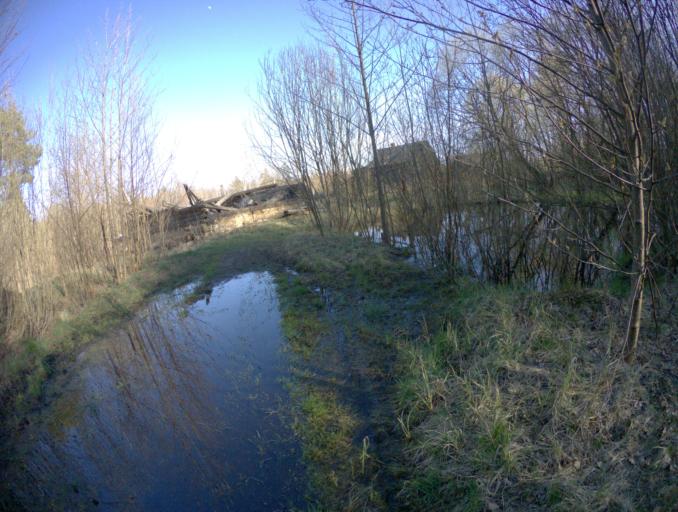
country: RU
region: Vladimir
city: Ivanishchi
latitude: 55.6672
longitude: 40.3881
